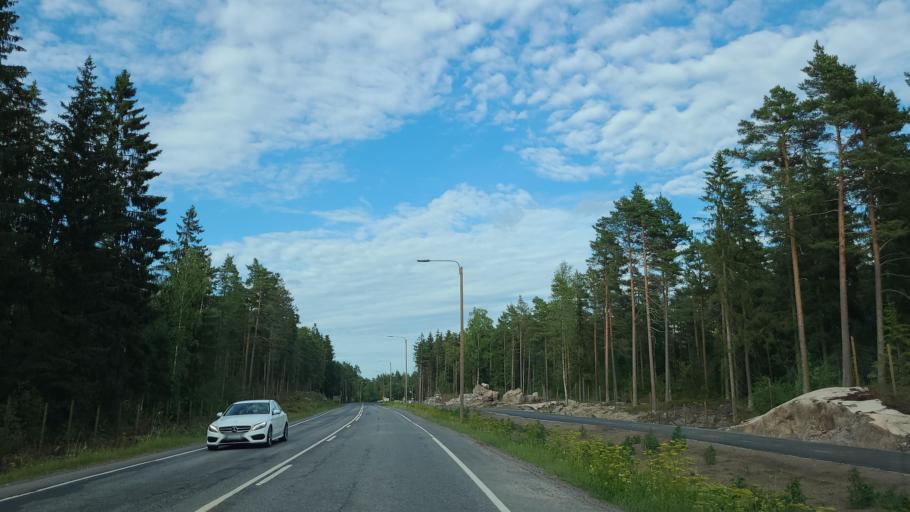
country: FI
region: Varsinais-Suomi
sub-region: Turku
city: Naantali
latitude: 60.4575
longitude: 22.0017
